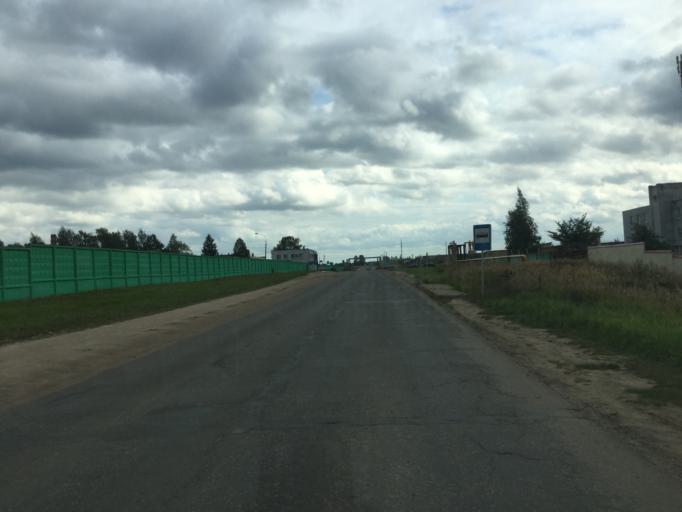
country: BY
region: Vitebsk
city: Vitebsk
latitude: 55.1606
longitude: 30.2616
